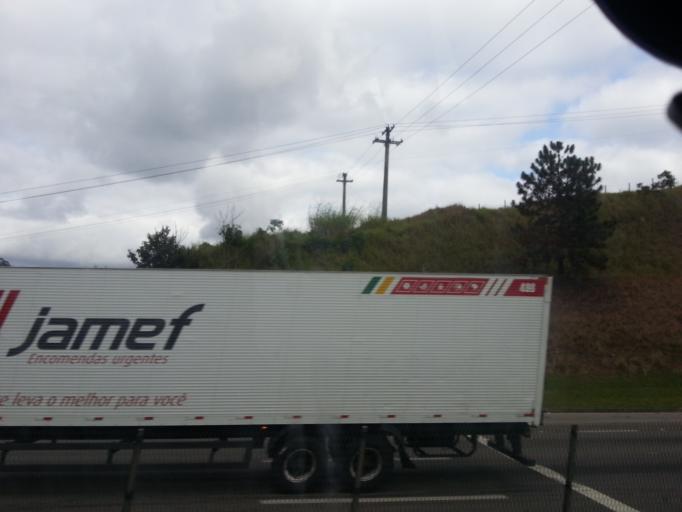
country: BR
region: Sao Paulo
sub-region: Aruja
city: Aruja
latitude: -23.4009
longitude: -46.3078
